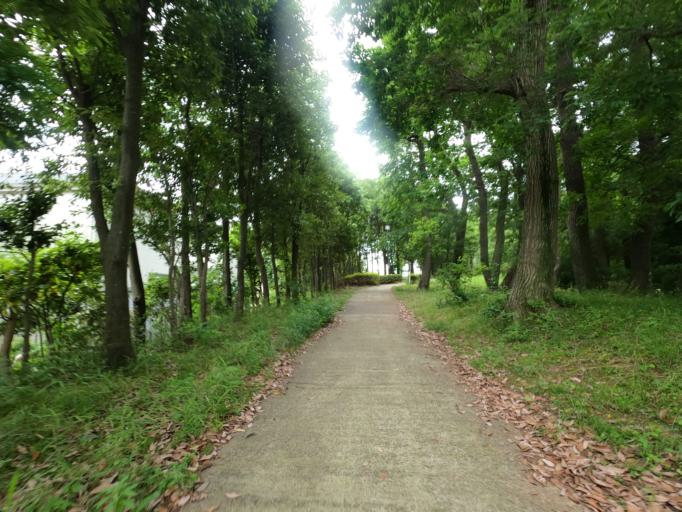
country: JP
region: Ibaraki
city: Moriya
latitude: 35.9598
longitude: 139.9629
